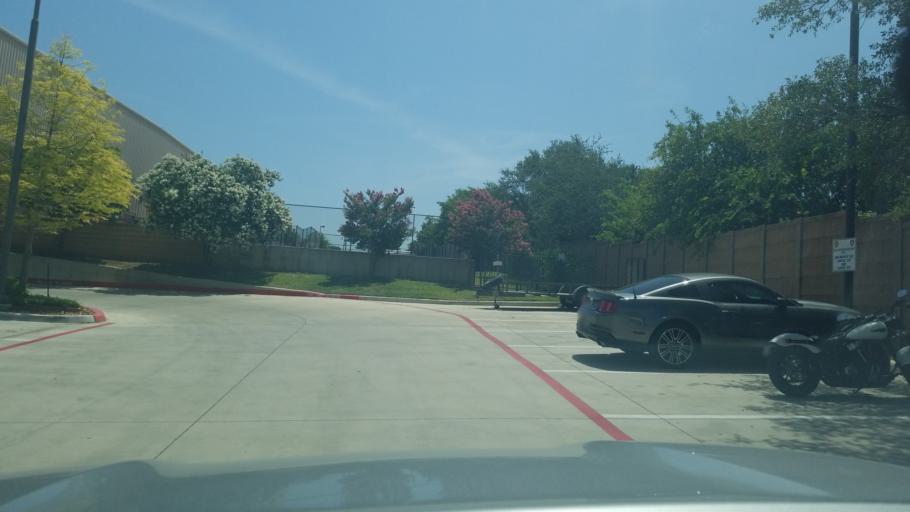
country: US
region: Texas
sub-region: Bexar County
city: Hollywood Park
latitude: 29.6088
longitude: -98.4799
